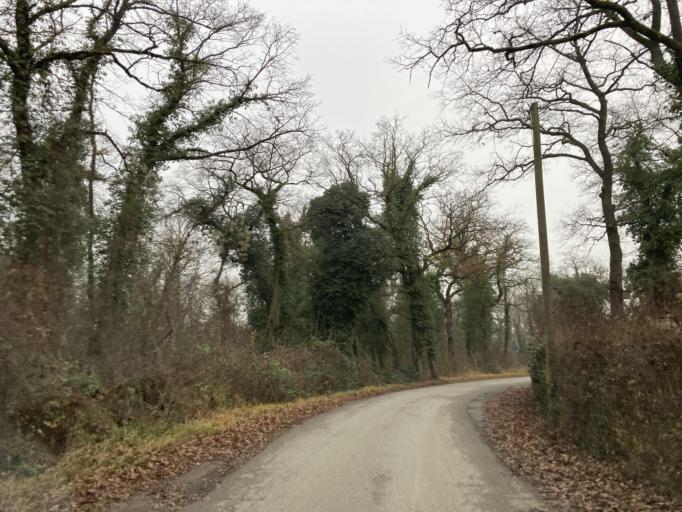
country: DE
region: Baden-Wuerttemberg
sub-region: Freiburg Region
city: Neuenburg am Rhein
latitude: 47.7940
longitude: 7.5466
